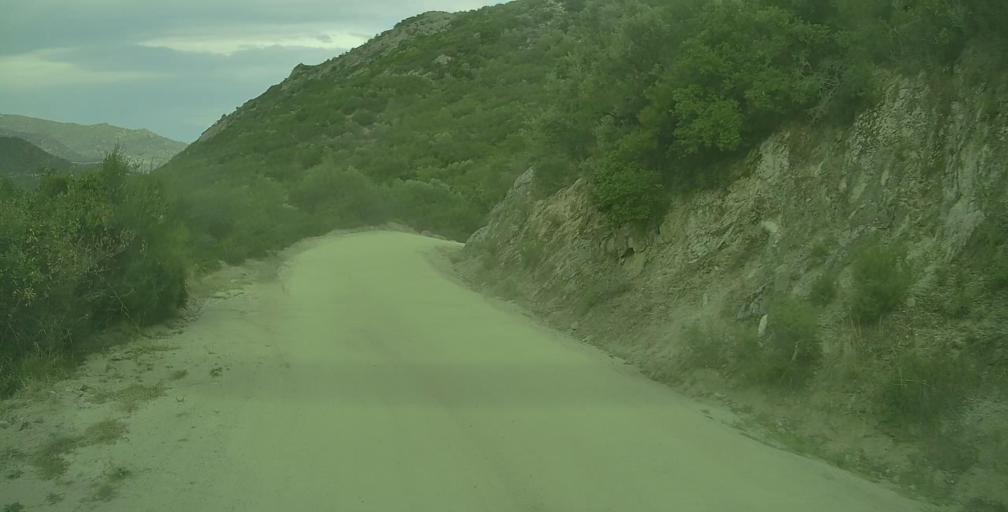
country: GR
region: Central Macedonia
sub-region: Nomos Chalkidikis
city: Sykia
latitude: 40.0122
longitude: 23.9389
